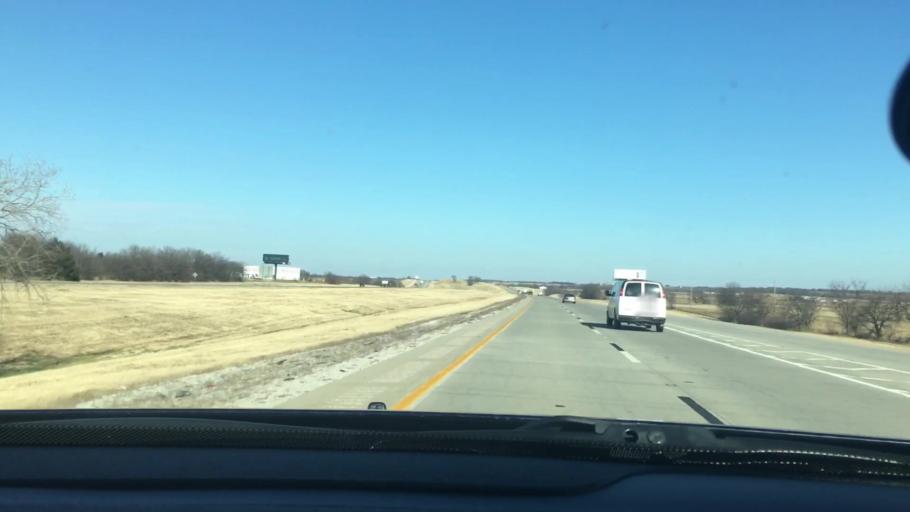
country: US
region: Oklahoma
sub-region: Carter County
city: Ardmore
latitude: 34.0734
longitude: -97.1495
